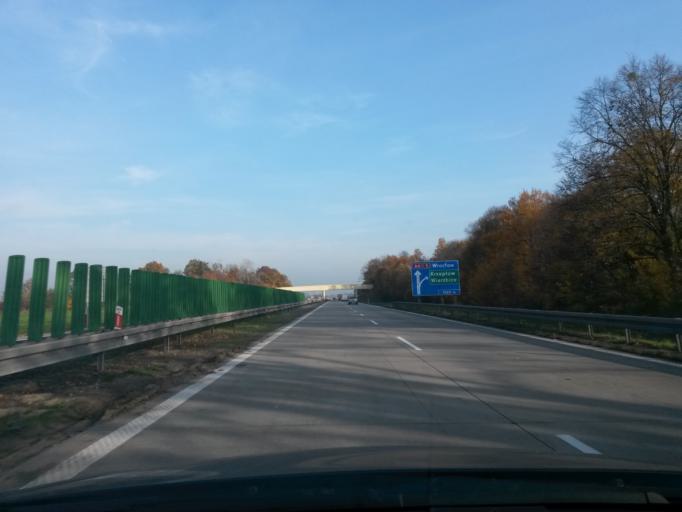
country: PL
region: Lower Silesian Voivodeship
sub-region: Powiat wroclawski
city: Smolec
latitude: 51.0356
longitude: 16.8685
